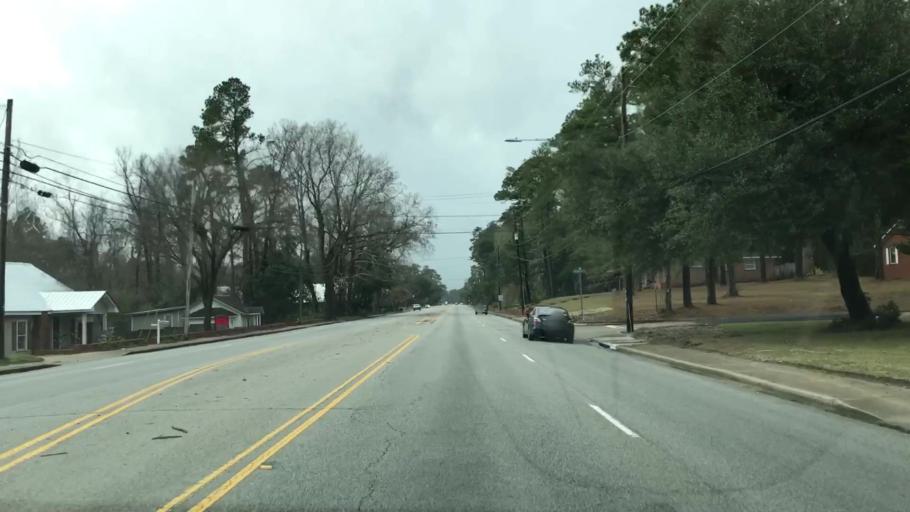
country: US
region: South Carolina
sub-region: Horry County
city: Conway
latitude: 33.8293
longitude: -79.0620
